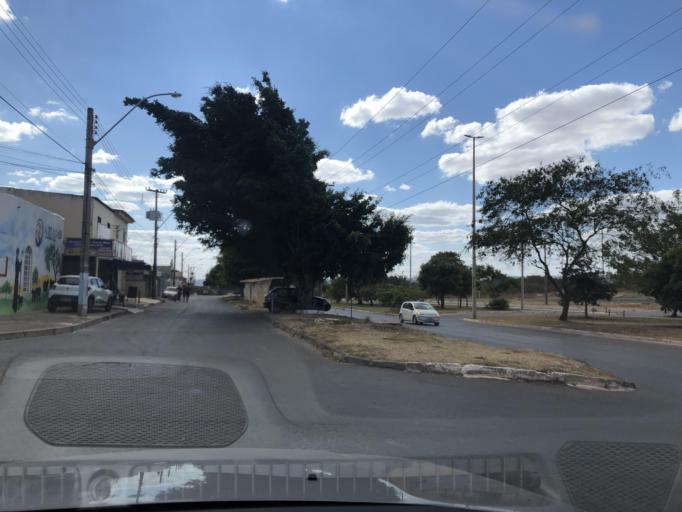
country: BR
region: Federal District
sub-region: Brasilia
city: Brasilia
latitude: -15.8927
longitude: -48.1395
